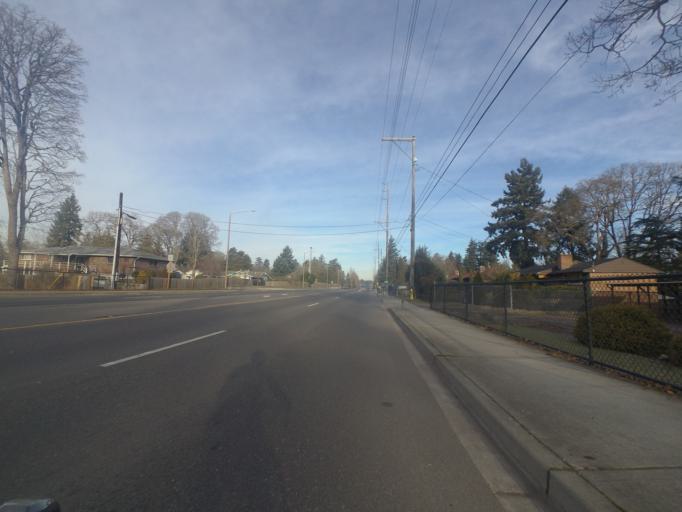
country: US
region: Washington
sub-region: Pierce County
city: Lakewood
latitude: 47.1808
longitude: -122.5181
